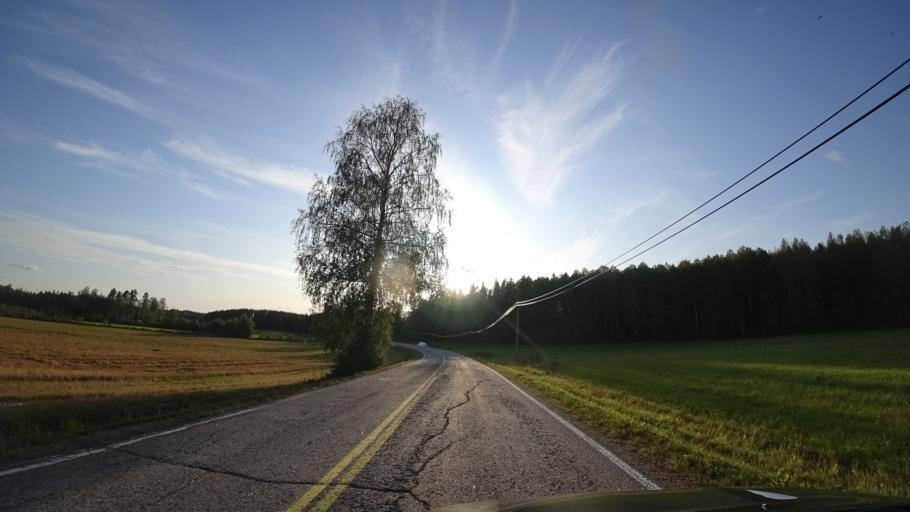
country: FI
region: Haeme
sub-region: Haemeenlinna
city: Tuulos
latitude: 61.0087
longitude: 24.8601
